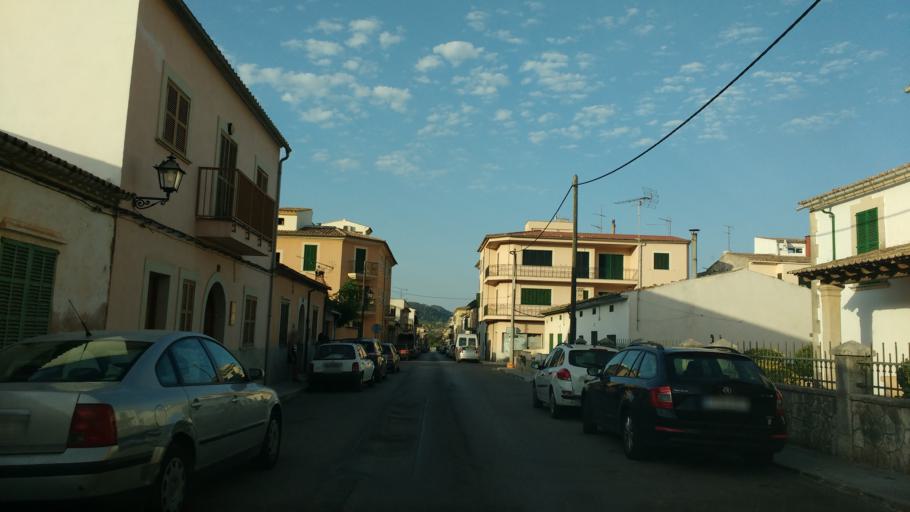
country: ES
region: Balearic Islands
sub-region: Illes Balears
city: Alaro
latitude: 39.7040
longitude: 2.7935
